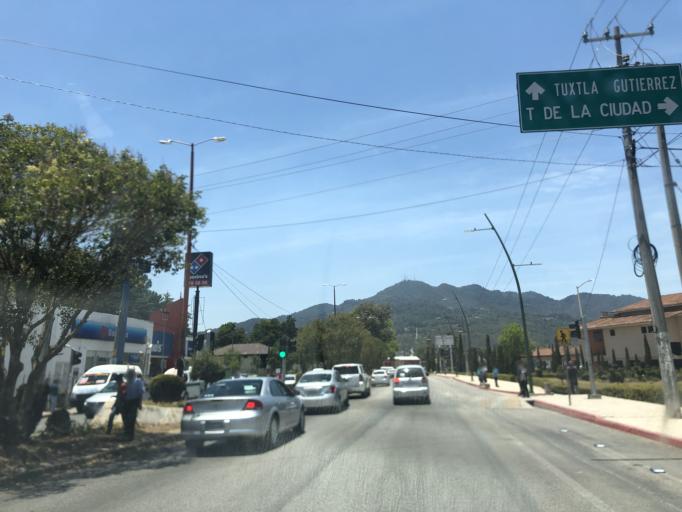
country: MX
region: Chiapas
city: San Cristobal de las Casas
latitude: 16.7322
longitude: -92.6507
